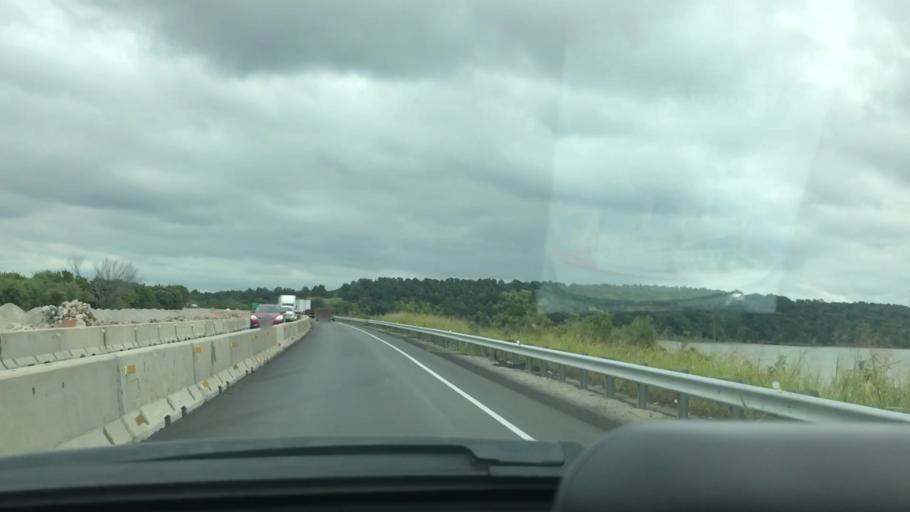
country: US
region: Oklahoma
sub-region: McIntosh County
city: Eufaula
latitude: 35.2419
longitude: -95.5867
